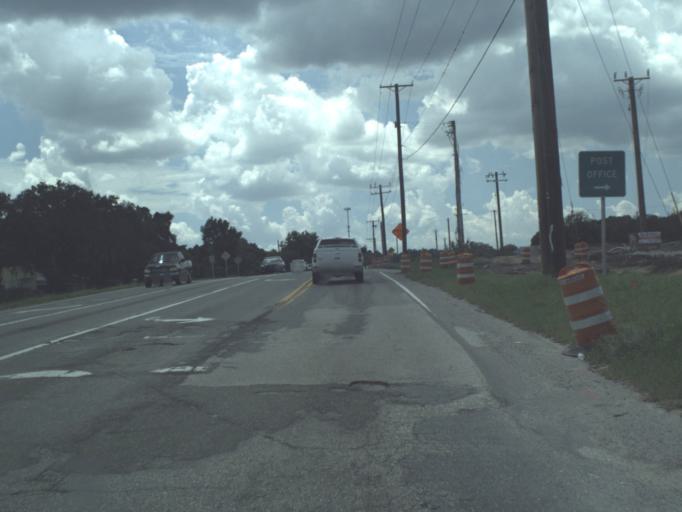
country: US
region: Florida
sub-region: Hillsborough County
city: Seffner
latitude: 27.9828
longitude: -82.2778
